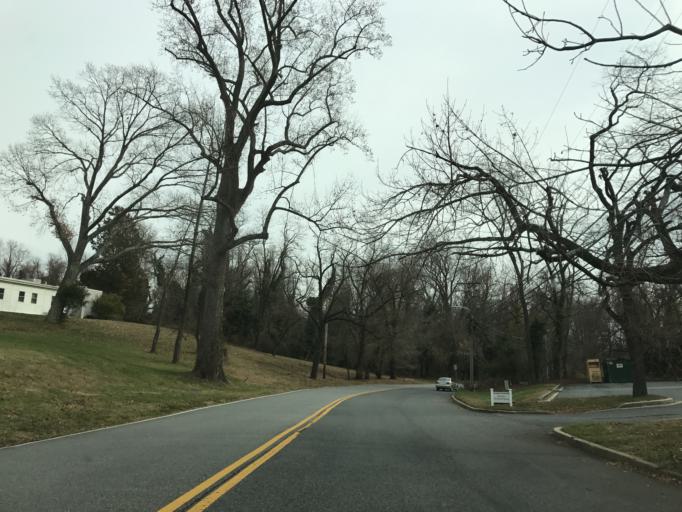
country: US
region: Maryland
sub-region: Anne Arundel County
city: Arnold
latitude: 39.0280
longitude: -76.5011
